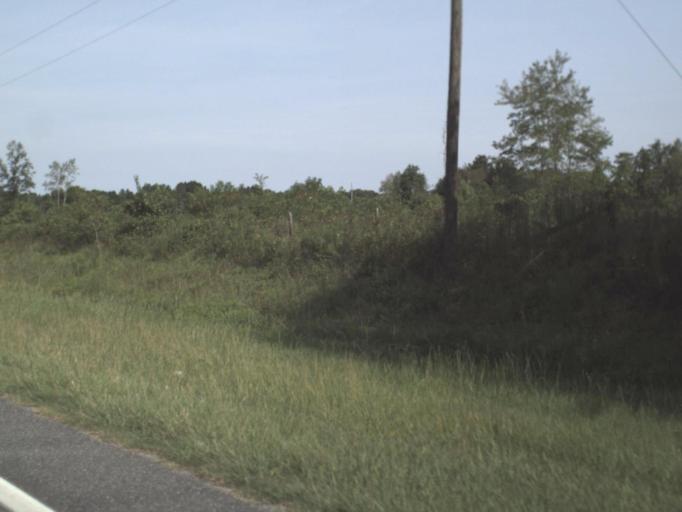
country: US
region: Florida
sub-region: Suwannee County
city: Wellborn
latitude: 30.3202
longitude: -82.7904
